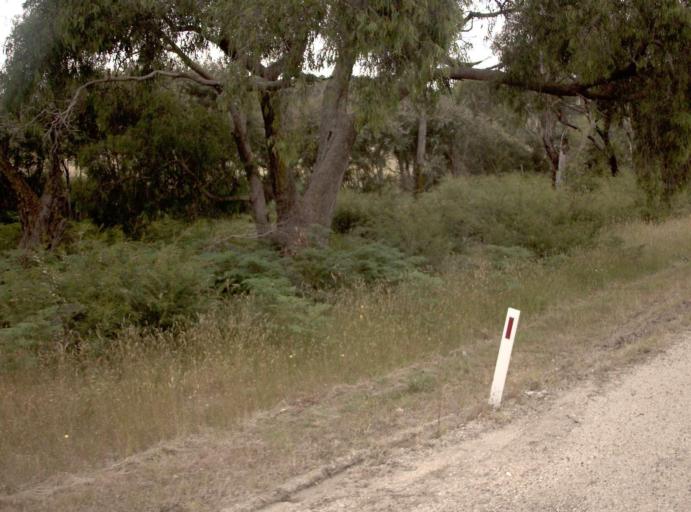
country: AU
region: Victoria
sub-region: Wellington
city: Sale
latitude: -38.1822
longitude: 147.1391
